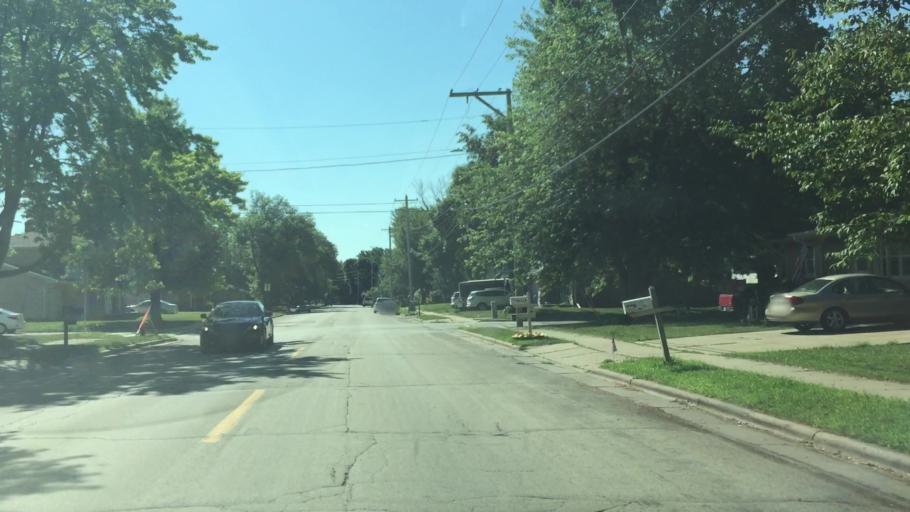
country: US
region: Wisconsin
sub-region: Winnebago County
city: Menasha
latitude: 44.2203
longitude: -88.4228
